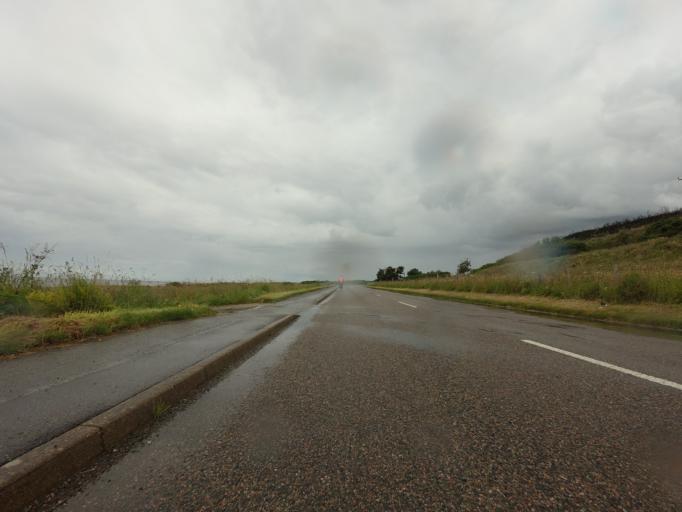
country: GB
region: Scotland
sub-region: Moray
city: Buckie
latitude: 57.6704
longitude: -2.9959
